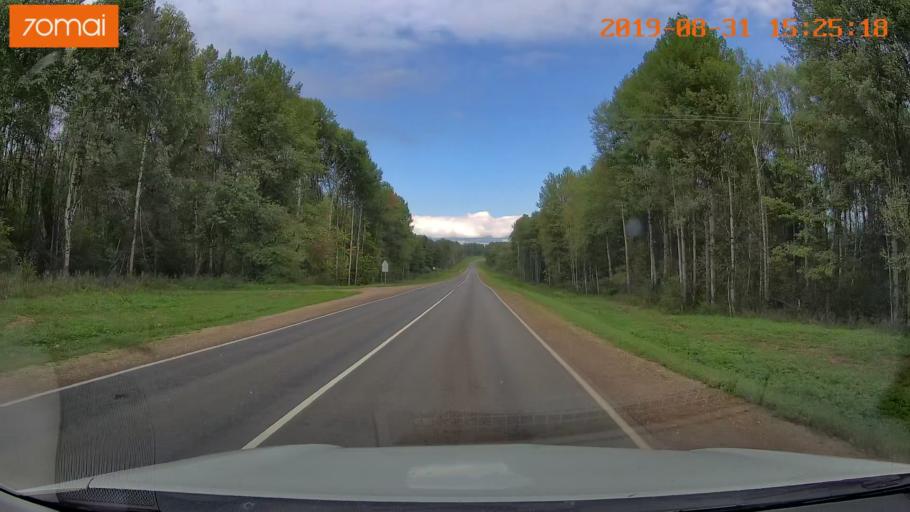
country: RU
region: Kaluga
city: Baryatino
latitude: 54.5394
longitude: 34.5175
